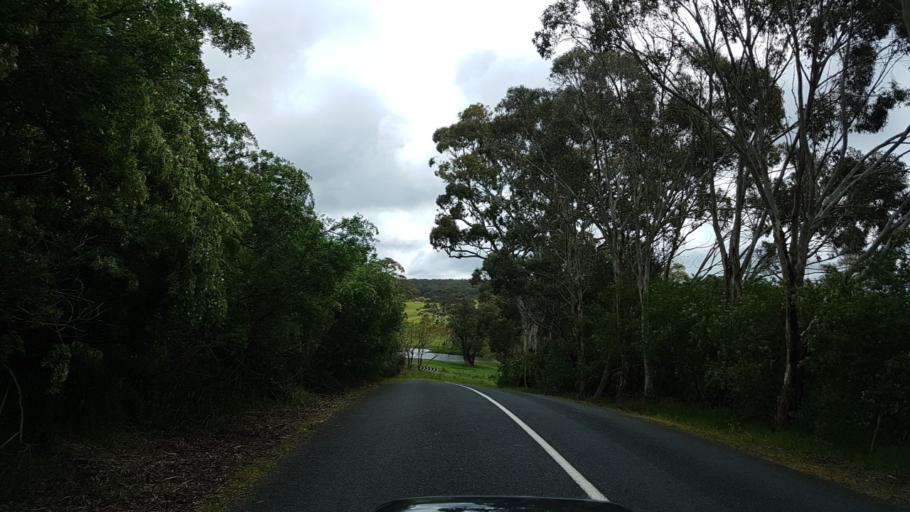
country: AU
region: South Australia
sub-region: Adelaide Hills
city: Lobethal
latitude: -34.8894
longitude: 138.8910
